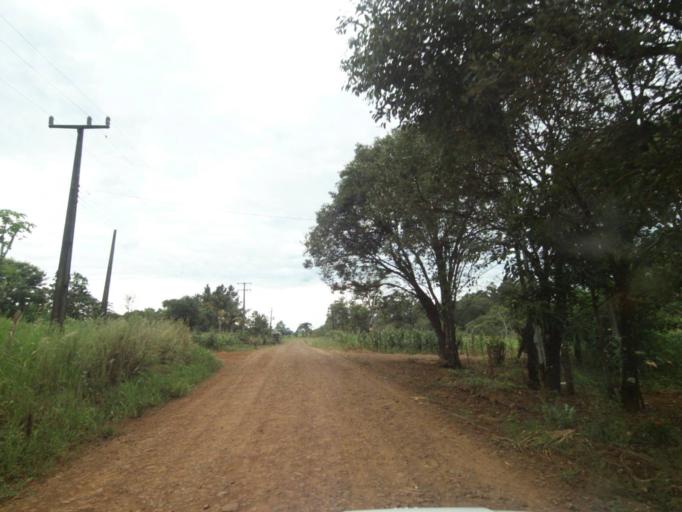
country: BR
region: Parana
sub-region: Guaraniacu
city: Guaraniacu
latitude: -24.9105
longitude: -52.9357
